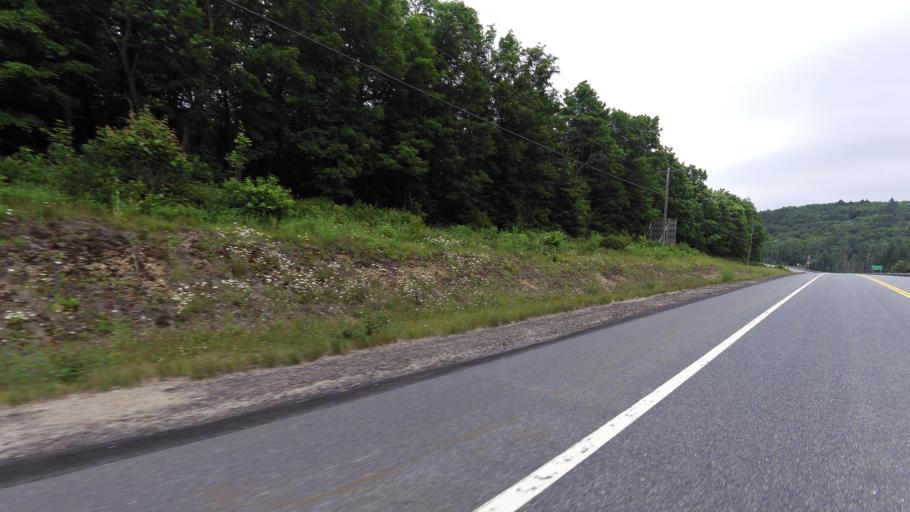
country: CA
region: Ontario
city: Huntsville
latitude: 45.3853
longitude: -78.9062
